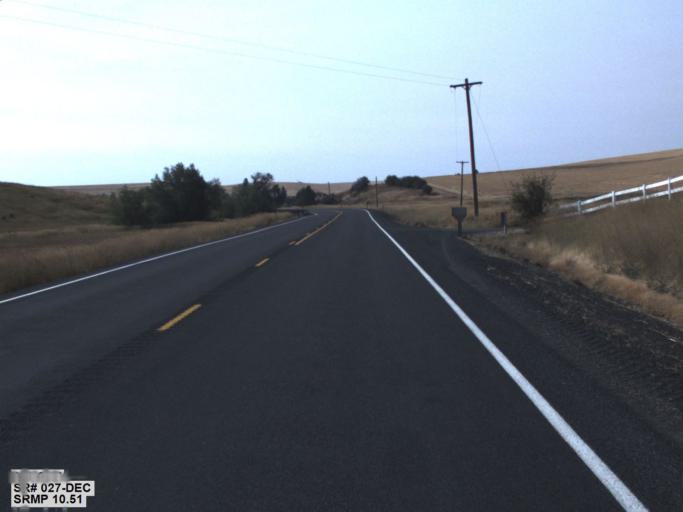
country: US
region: Washington
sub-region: Whitman County
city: Pullman
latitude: 46.8629
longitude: -117.1301
